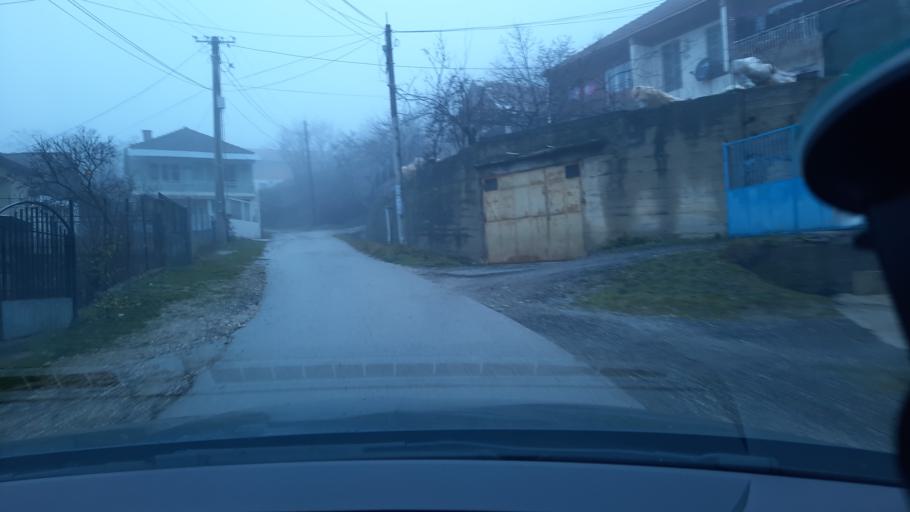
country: MK
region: Vrapciste
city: Vrapciste
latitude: 41.8416
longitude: 20.8780
